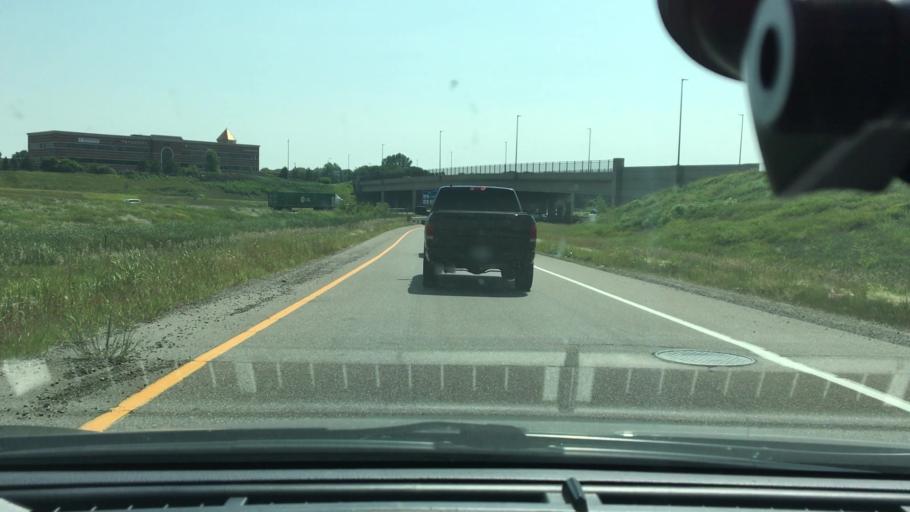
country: US
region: Minnesota
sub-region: Hennepin County
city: Maple Grove
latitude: 45.1259
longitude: -93.4865
